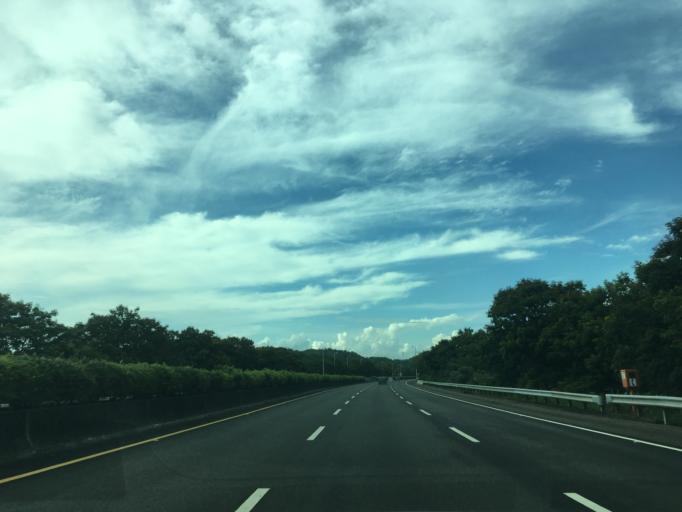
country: TW
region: Taiwan
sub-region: Chiayi
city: Jiayi Shi
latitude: 23.5179
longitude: 120.4848
